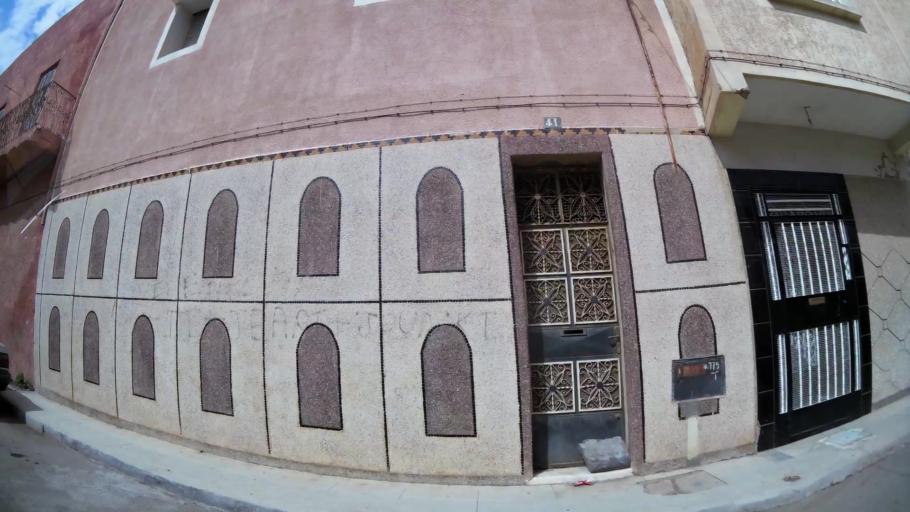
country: MA
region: Oriental
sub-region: Oujda-Angad
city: Oujda
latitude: 34.6853
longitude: -1.9120
